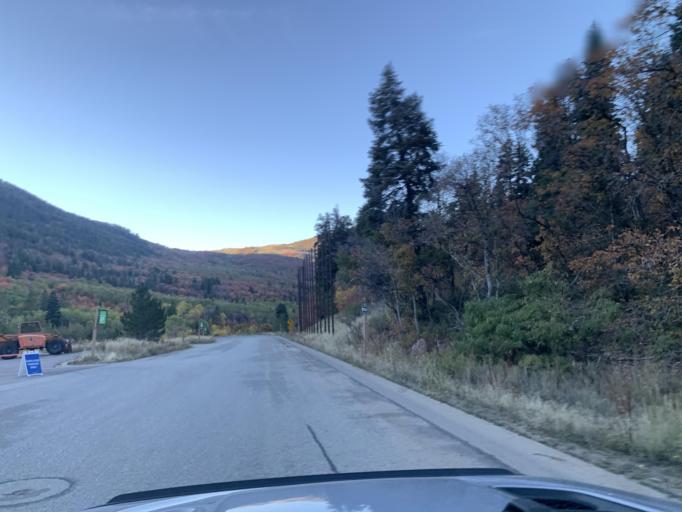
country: US
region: Utah
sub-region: Weber County
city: Uintah
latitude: 41.2174
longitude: -111.8604
